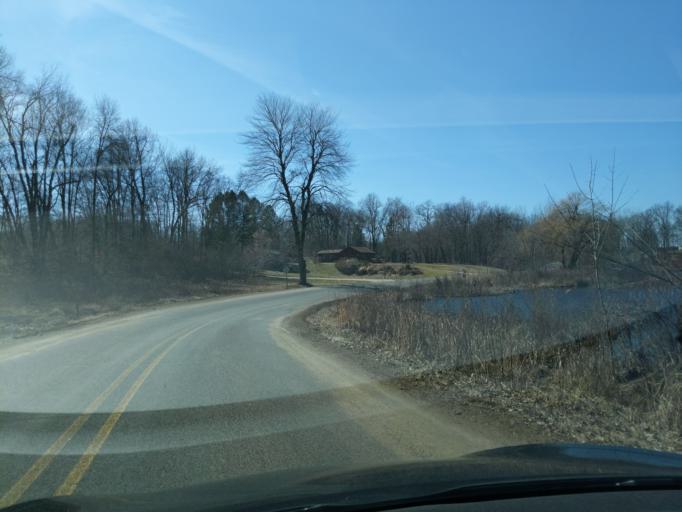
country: US
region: Michigan
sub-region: Ionia County
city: Lake Odessa
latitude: 42.7121
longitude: -85.0822
